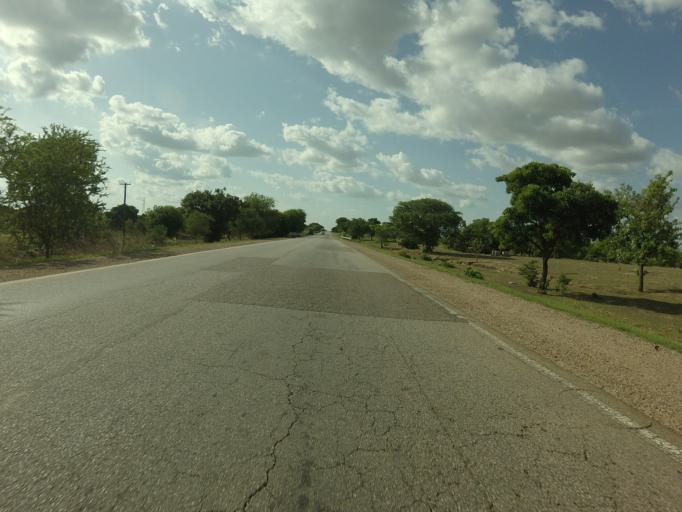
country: GH
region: Upper East
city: Bolgatanga
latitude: 10.6576
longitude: -0.8589
